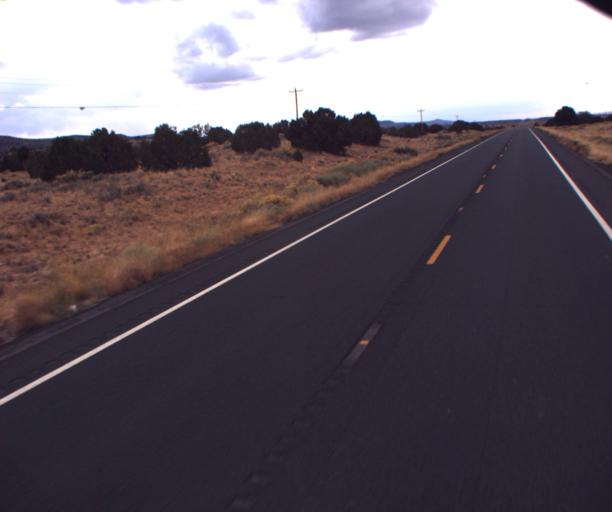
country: US
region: Arizona
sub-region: Coconino County
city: Kaibito
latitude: 36.4744
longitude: -110.6607
